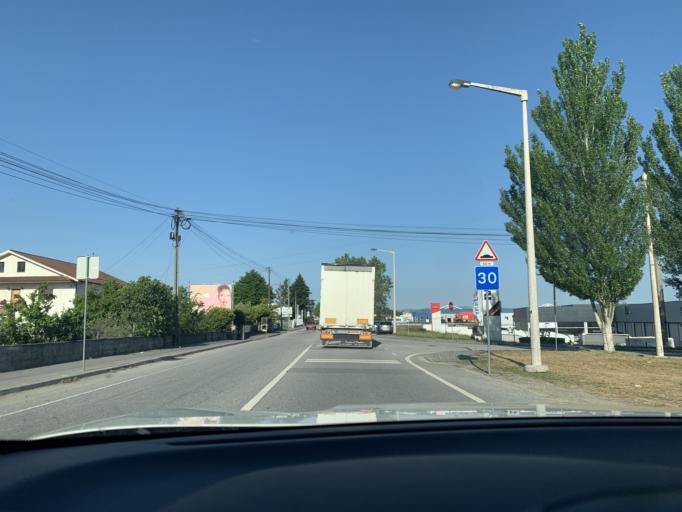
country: PT
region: Viseu
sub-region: Viseu
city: Rio de Loba
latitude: 40.6281
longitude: -7.8700
